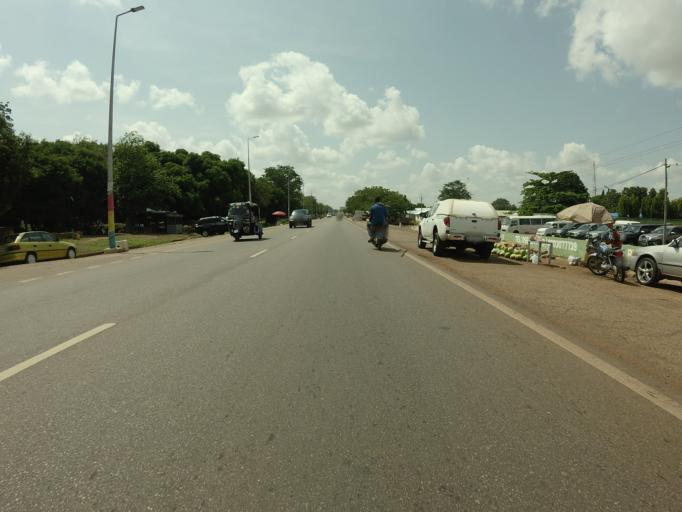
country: GH
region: Northern
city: Tamale
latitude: 9.4445
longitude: -0.8443
